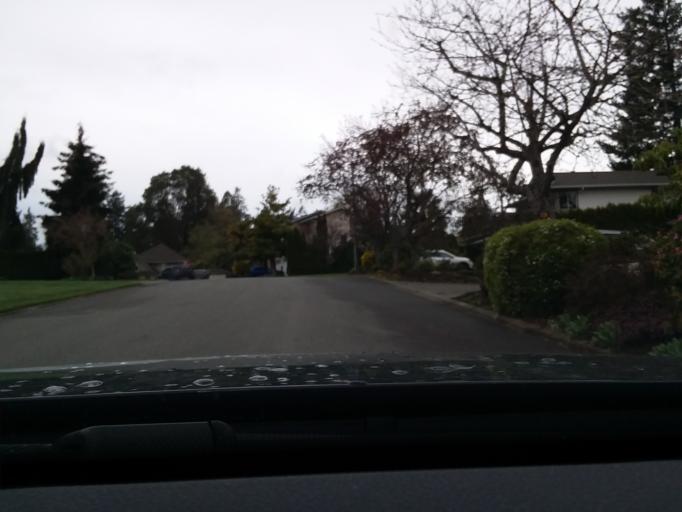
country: CA
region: British Columbia
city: Victoria
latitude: 48.5197
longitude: -123.3802
